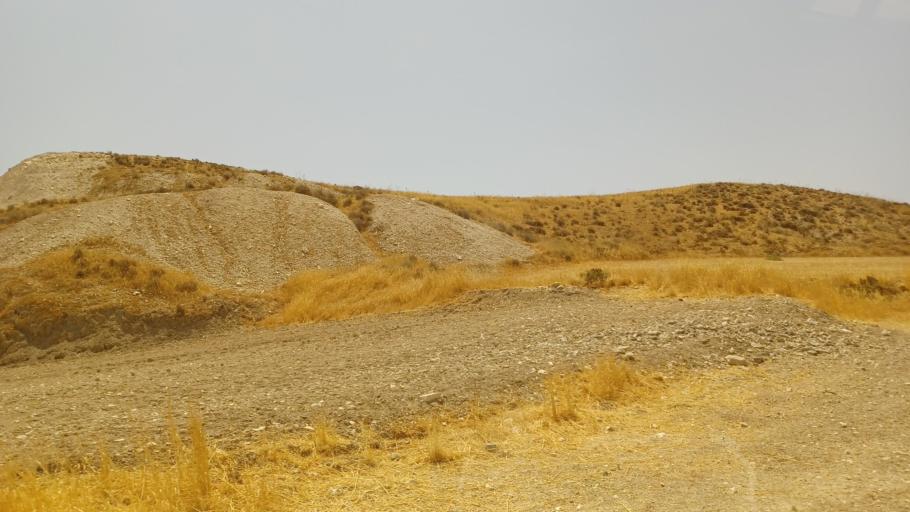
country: CY
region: Larnaka
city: Troulloi
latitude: 35.0323
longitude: 33.5970
